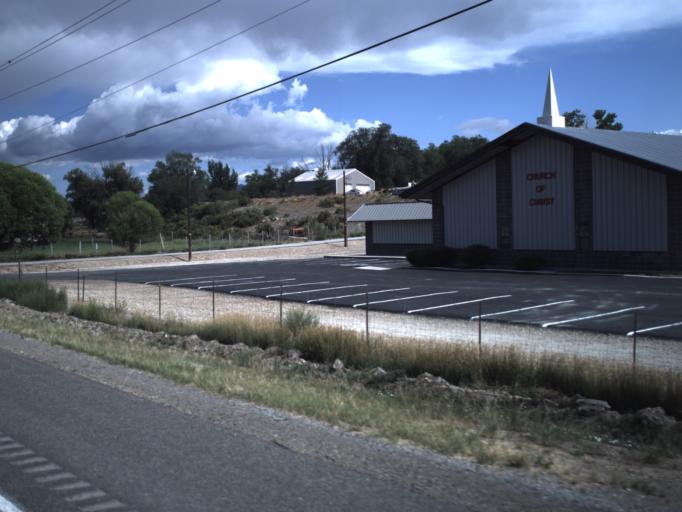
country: US
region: Utah
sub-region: Carbon County
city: Wellington
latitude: 39.5530
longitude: -110.7562
